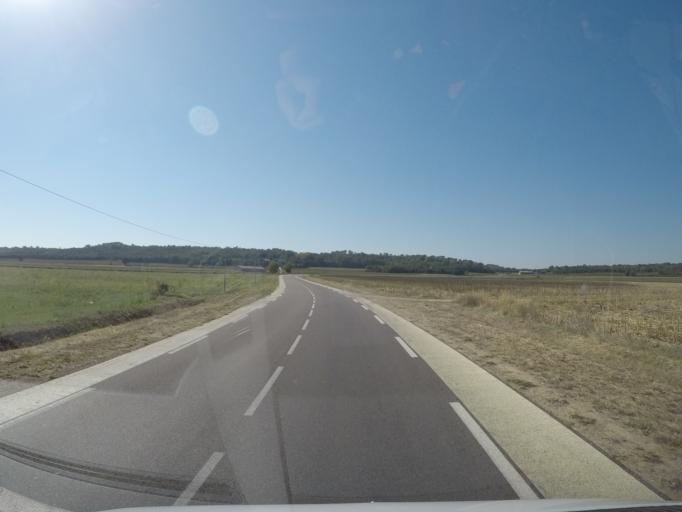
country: FR
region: Languedoc-Roussillon
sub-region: Departement du Gard
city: Uzes
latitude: 43.9968
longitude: 4.3933
